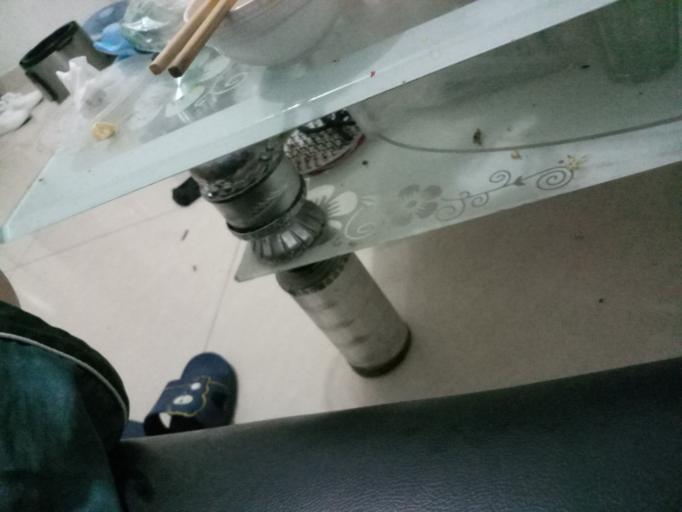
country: CN
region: Sichuan
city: Chengdu
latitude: 30.5509
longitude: 104.1005
